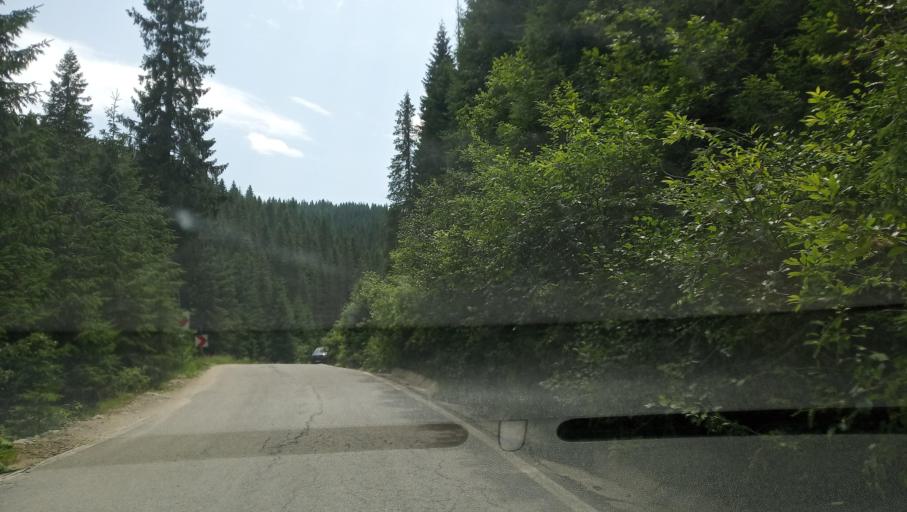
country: RO
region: Dambovita
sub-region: Comuna Moroeni
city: Glod
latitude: 45.3267
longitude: 25.4340
